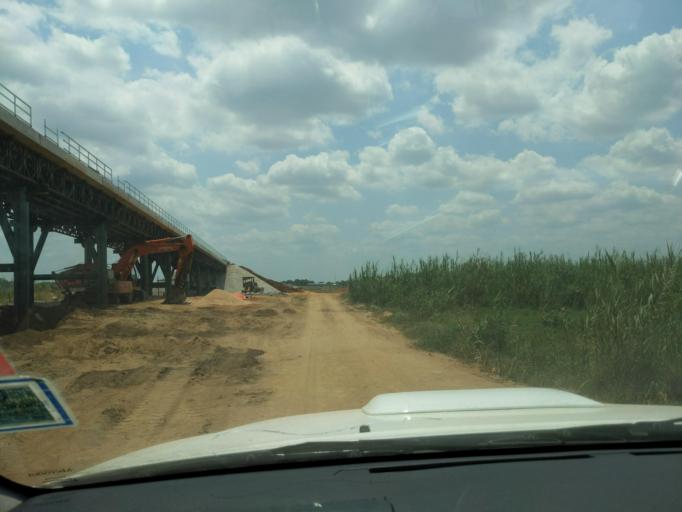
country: MZ
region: Zambezia
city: Quelimane
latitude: -17.2564
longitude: 37.0756
